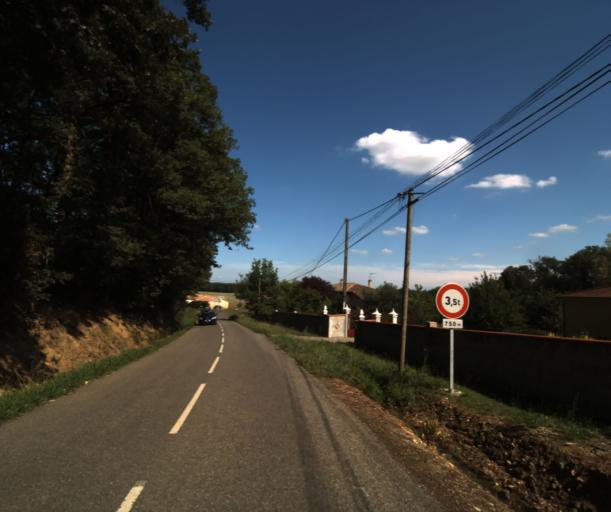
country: FR
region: Midi-Pyrenees
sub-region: Departement de la Haute-Garonne
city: Fonsorbes
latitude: 43.5005
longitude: 1.2186
